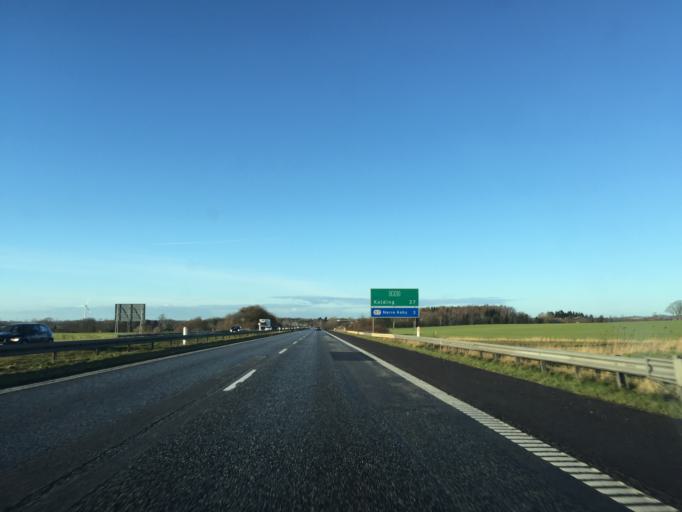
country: DK
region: South Denmark
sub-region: Middelfart Kommune
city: Ejby
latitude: 55.4581
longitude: 9.9322
